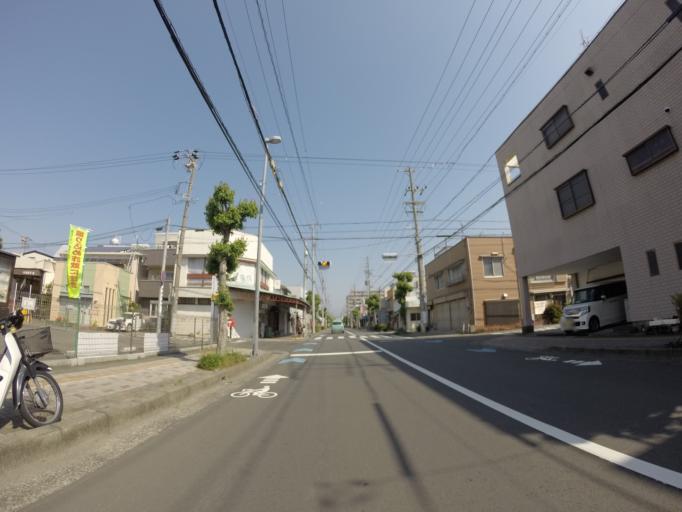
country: JP
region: Shizuoka
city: Shizuoka-shi
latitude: 35.0111
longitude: 138.4843
